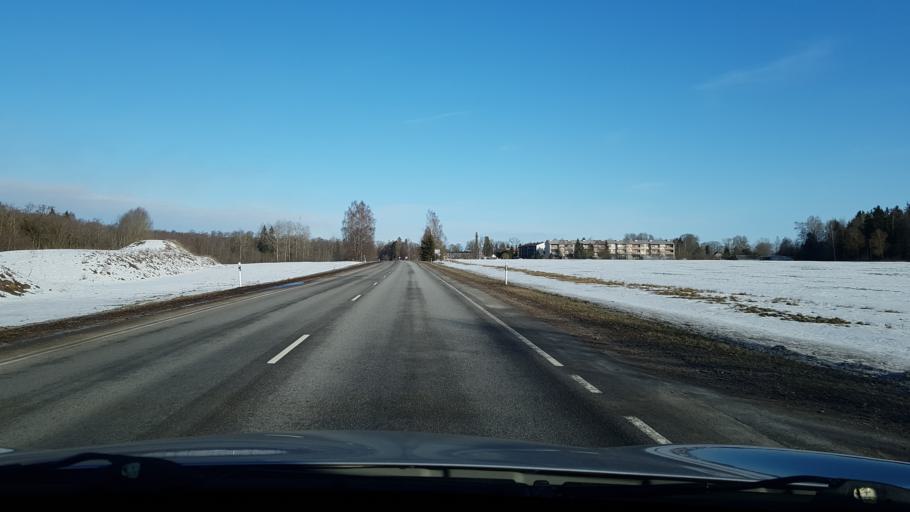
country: EE
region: Jogevamaa
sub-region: Poltsamaa linn
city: Poltsamaa
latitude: 58.7266
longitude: 25.7646
